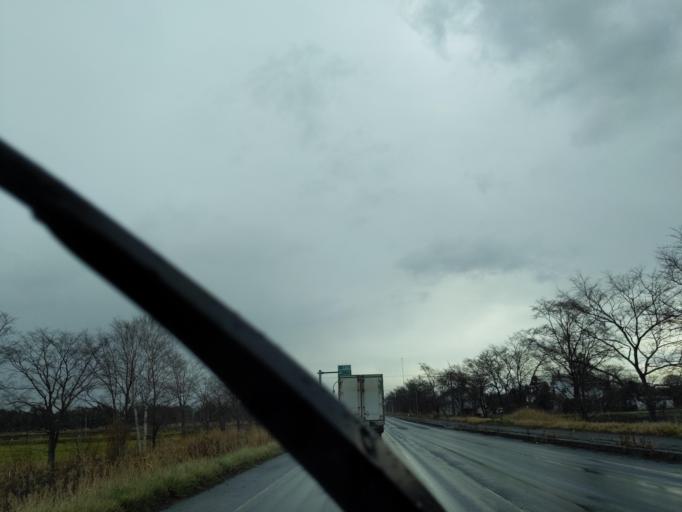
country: JP
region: Hokkaido
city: Ebetsu
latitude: 43.1086
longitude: 141.5931
